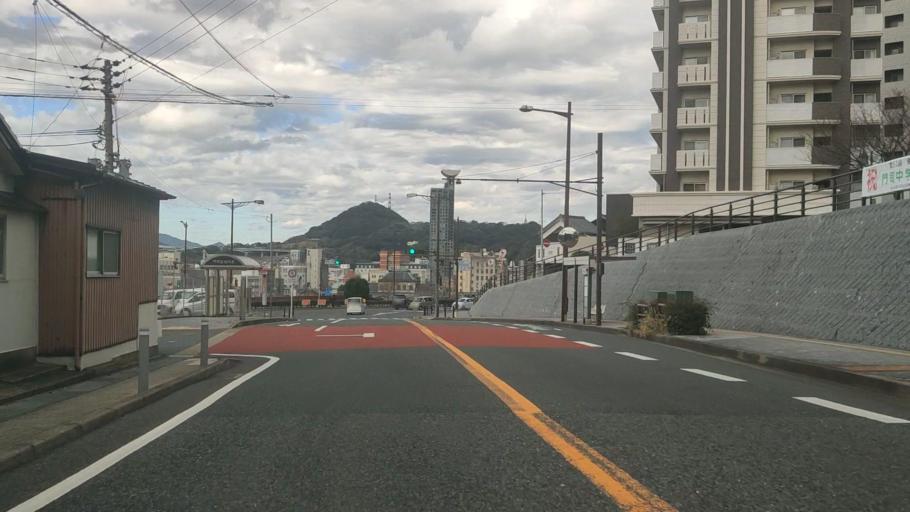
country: JP
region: Yamaguchi
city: Shimonoseki
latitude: 33.9413
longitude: 130.9591
